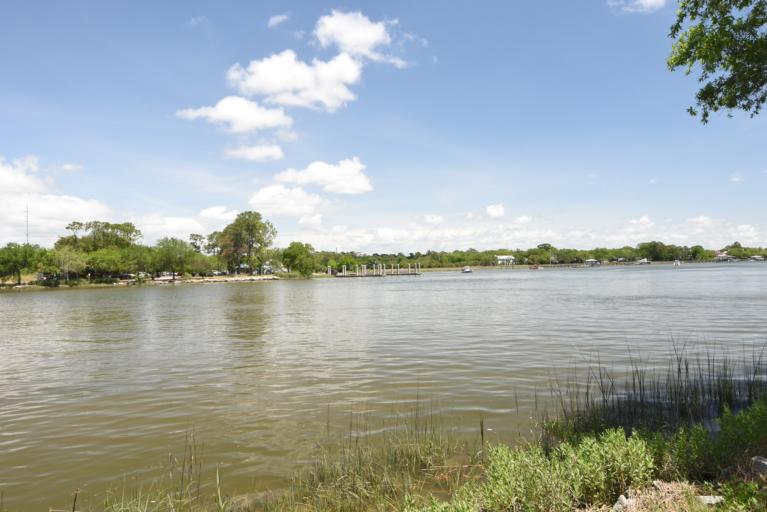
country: US
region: South Carolina
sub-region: Charleston County
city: Charleston
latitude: 32.7659
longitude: -79.9732
